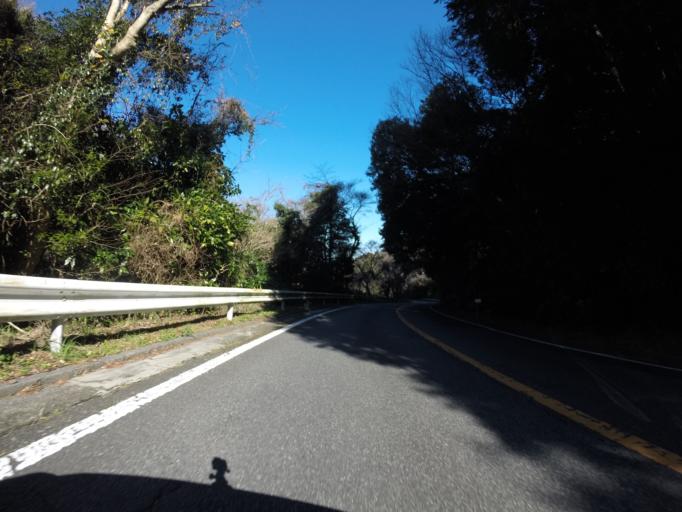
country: JP
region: Shizuoka
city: Shizuoka-shi
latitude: 34.9727
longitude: 138.4755
